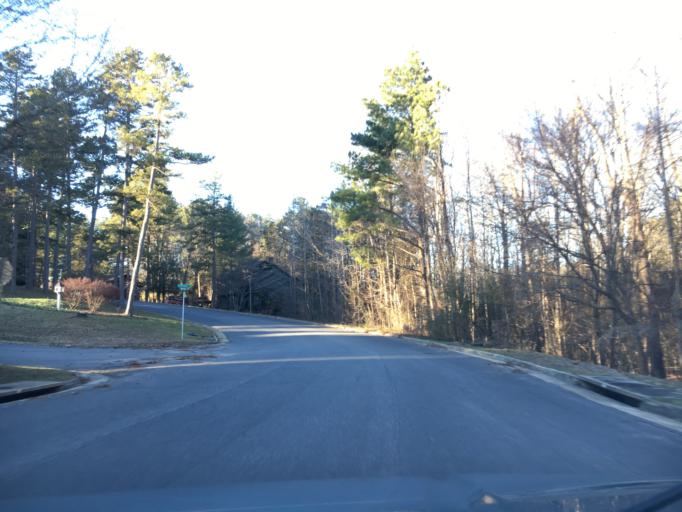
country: US
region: Virginia
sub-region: Halifax County
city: South Boston
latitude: 36.7059
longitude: -78.8819
